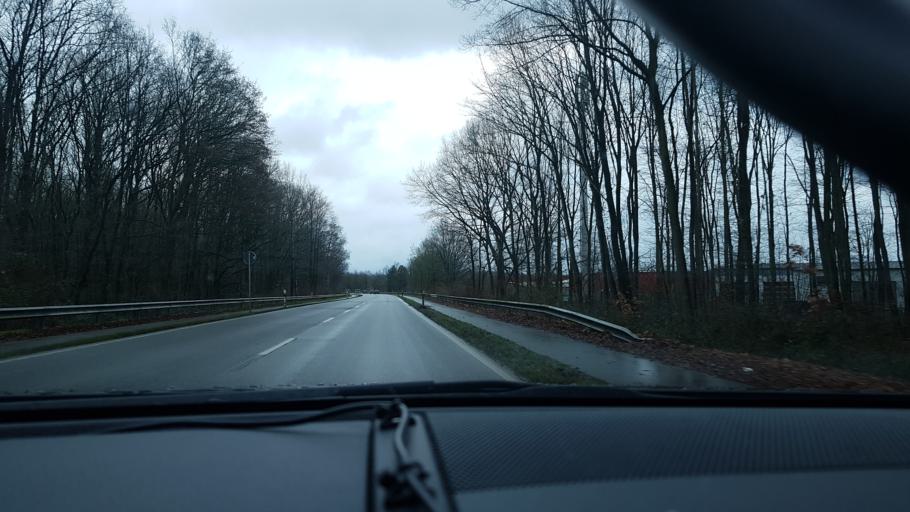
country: DE
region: North Rhine-Westphalia
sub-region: Regierungsbezirk Dusseldorf
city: Bruggen
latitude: 51.2506
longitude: 6.1878
